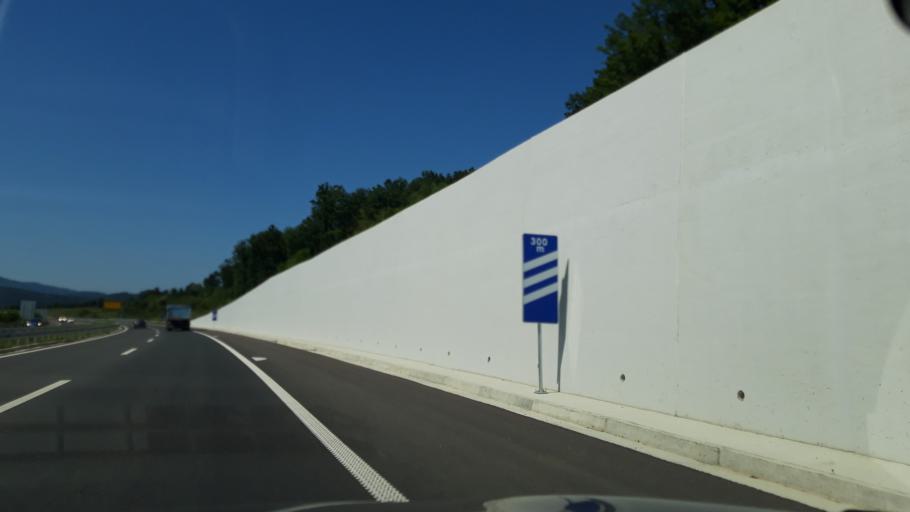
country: RS
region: Central Serbia
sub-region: Pcinjski Okrug
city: Vladicin Han
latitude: 42.6969
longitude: 22.0762
